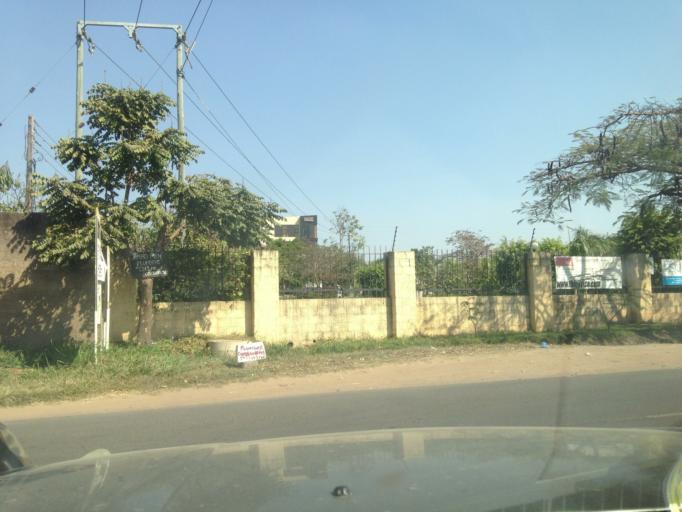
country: ZM
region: Lusaka
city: Lusaka
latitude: -15.3854
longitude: 28.3238
